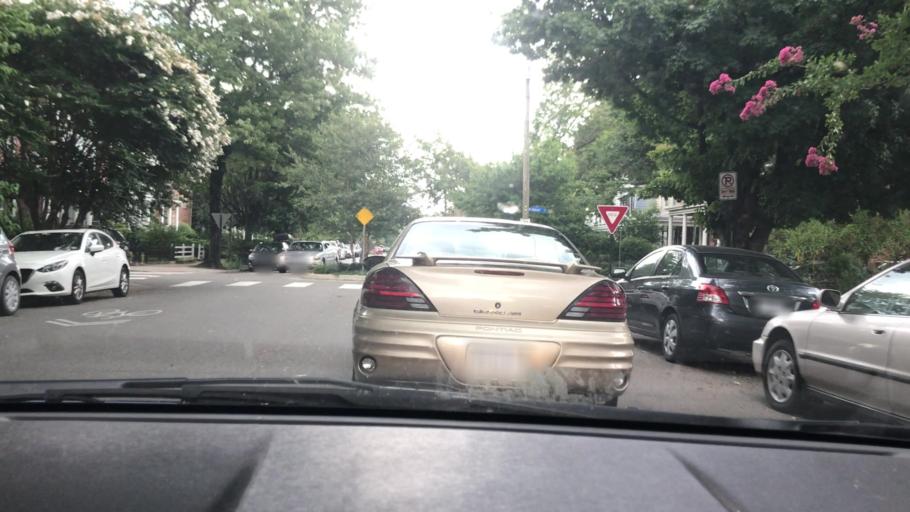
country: US
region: Virginia
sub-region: City of Richmond
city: Richmond
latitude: 37.5566
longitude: -77.4829
